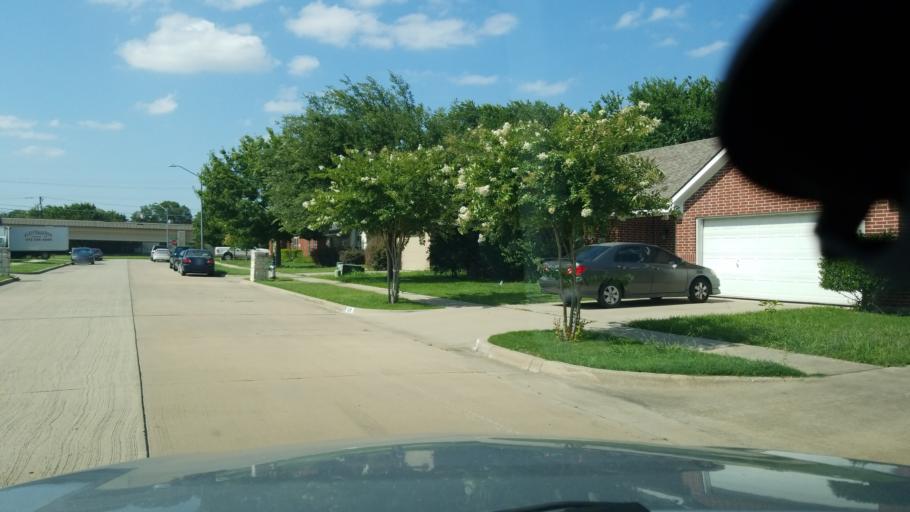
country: US
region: Texas
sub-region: Dallas County
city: Irving
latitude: 32.8141
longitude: -96.9727
